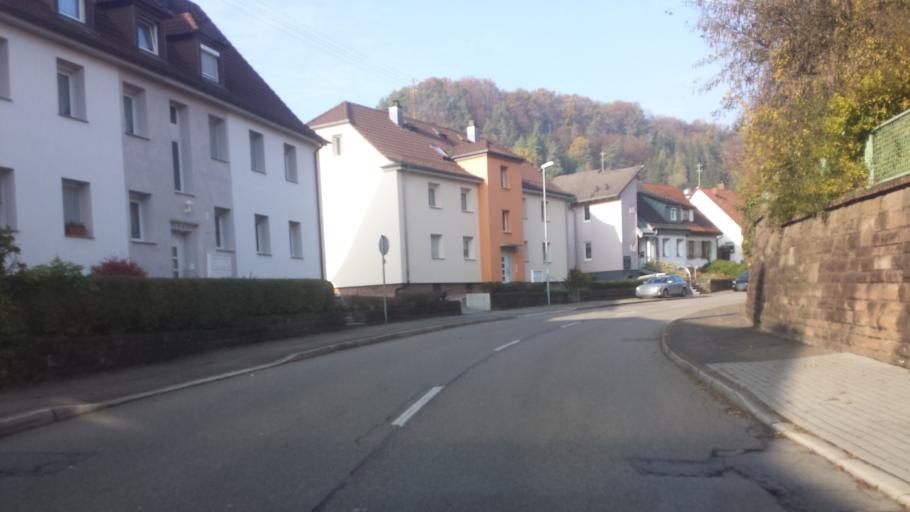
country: DE
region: Baden-Wuerttemberg
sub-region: Karlsruhe Region
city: Mosbach
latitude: 49.3501
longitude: 9.1313
